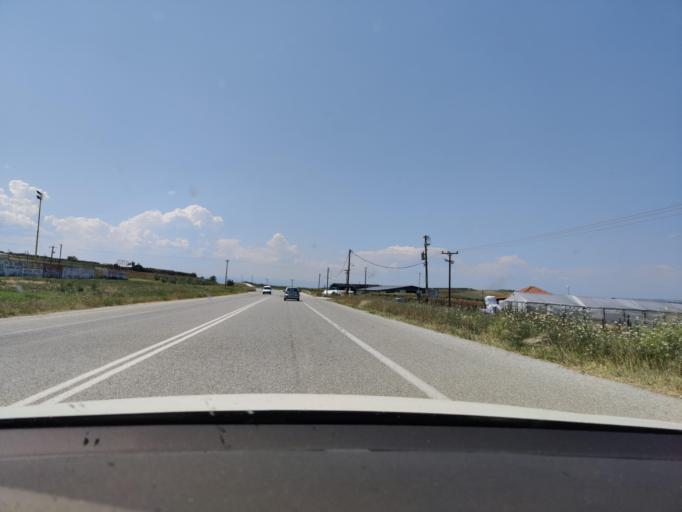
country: GR
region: Central Macedonia
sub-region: Nomos Serron
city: Draviskos
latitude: 40.9332
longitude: 23.8693
